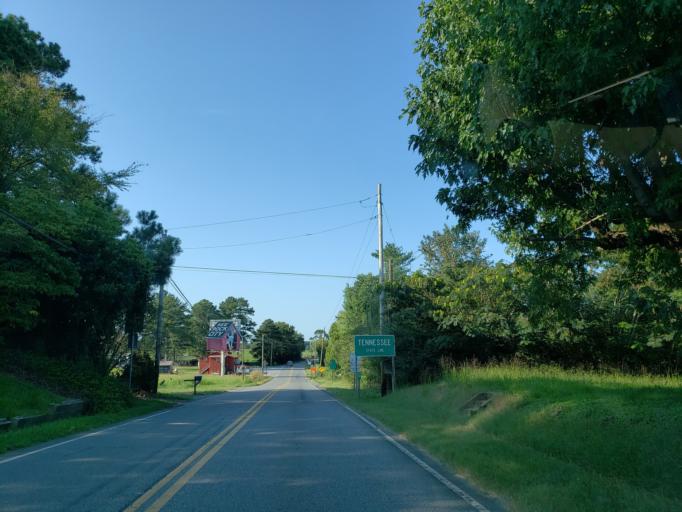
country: US
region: Tennessee
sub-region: Bradley County
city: Wildwood Lake
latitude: 34.9876
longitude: -84.7385
